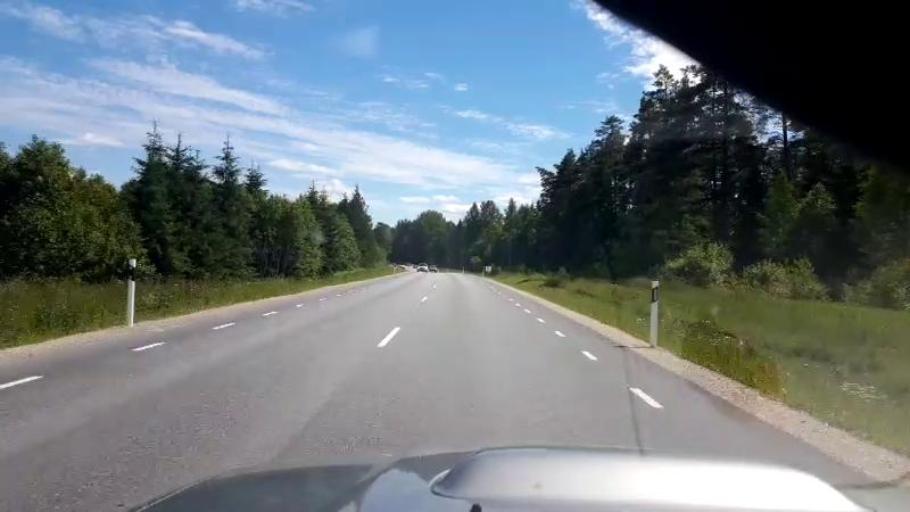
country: EE
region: Jogevamaa
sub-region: Jogeva linn
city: Jogeva
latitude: 58.7897
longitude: 26.3113
